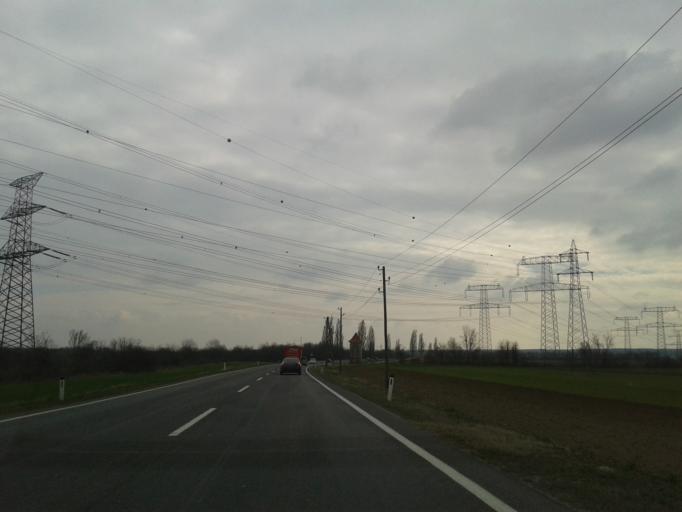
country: AT
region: Lower Austria
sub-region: Politischer Bezirk Wien-Umgebung
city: Fischamend Dorf
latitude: 48.1152
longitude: 16.6479
